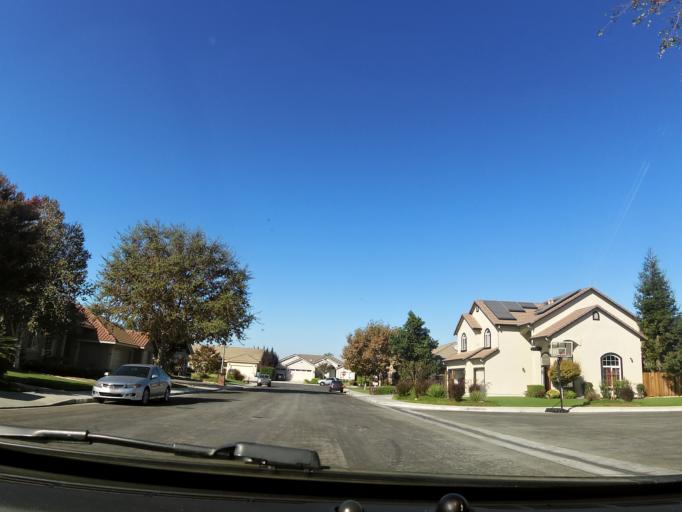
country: US
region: California
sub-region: San Benito County
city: Hollister
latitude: 36.8331
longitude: -121.3935
